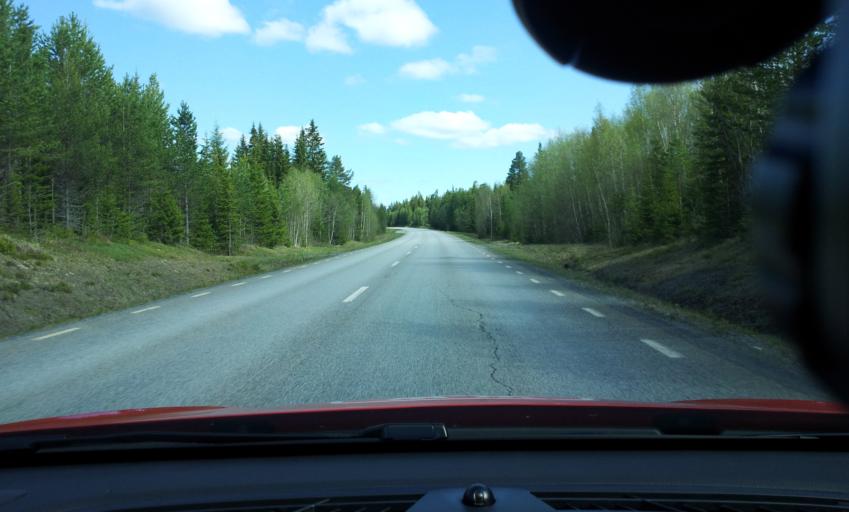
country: SE
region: Jaemtland
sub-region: Krokoms Kommun
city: Valla
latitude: 63.2948
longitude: 13.9268
